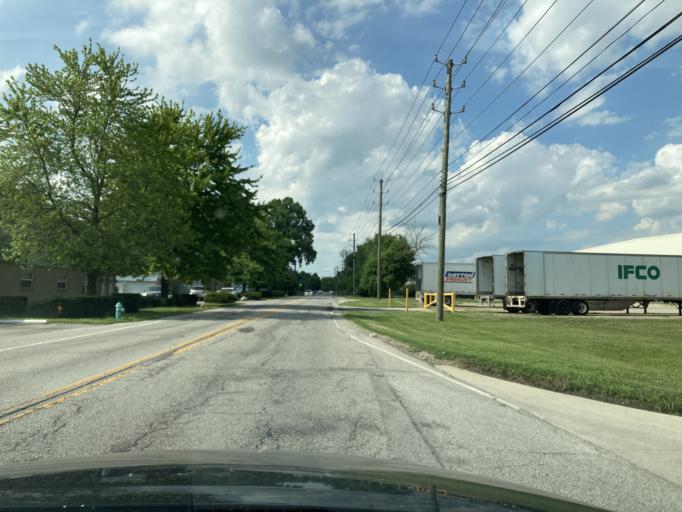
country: US
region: Indiana
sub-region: Marion County
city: Speedway
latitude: 39.8612
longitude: -86.2317
